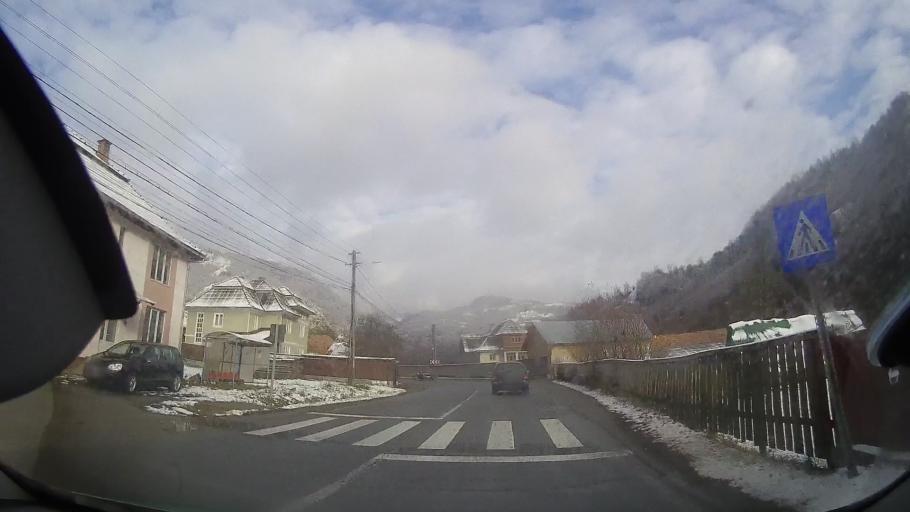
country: RO
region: Alba
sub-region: Oras Baia de Aries
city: Baia de Aries
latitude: 46.3927
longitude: 23.3001
